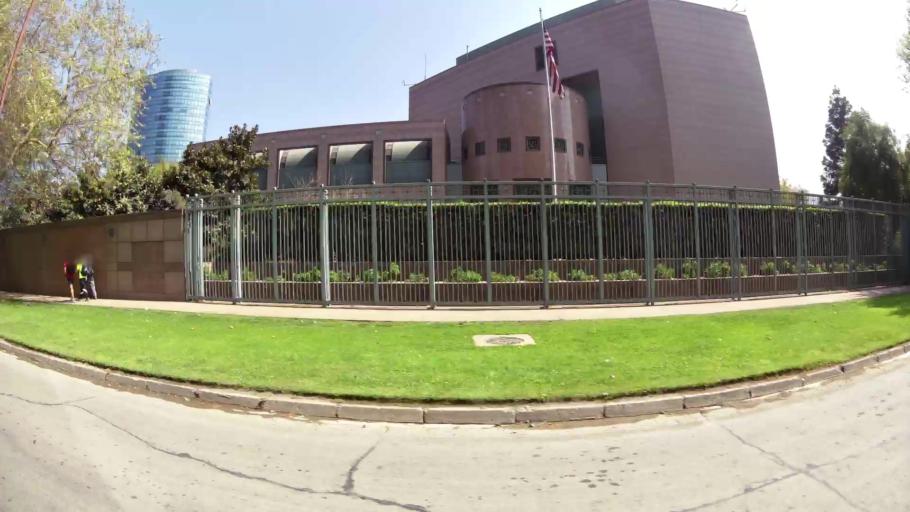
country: CL
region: Santiago Metropolitan
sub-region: Provincia de Santiago
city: Villa Presidente Frei, Nunoa, Santiago, Chile
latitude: -33.4122
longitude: -70.6039
